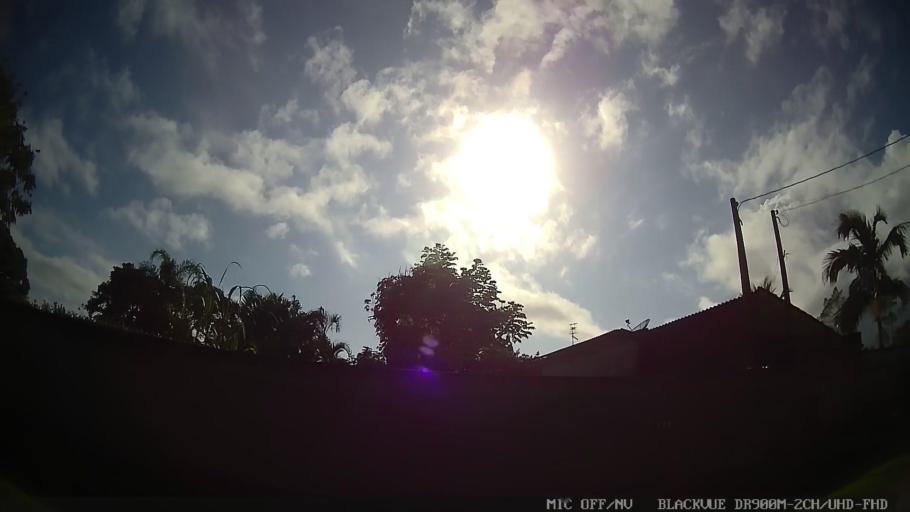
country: BR
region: Sao Paulo
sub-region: Itanhaem
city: Itanhaem
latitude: -24.2164
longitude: -46.8783
